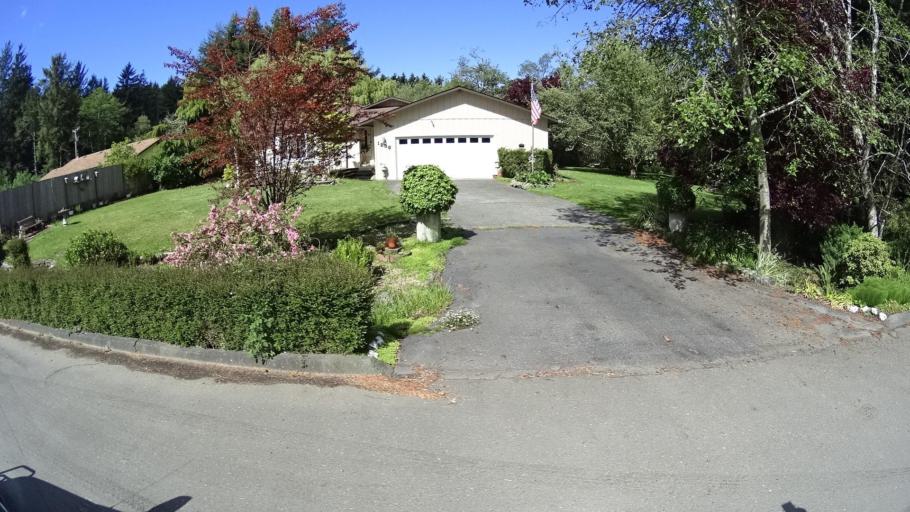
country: US
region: California
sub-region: Humboldt County
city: McKinleyville
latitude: 40.9276
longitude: -124.0814
